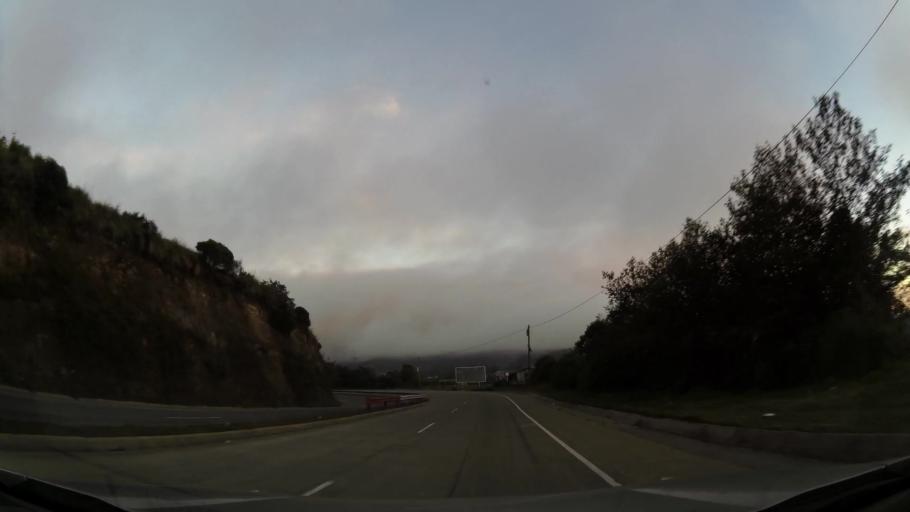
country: GT
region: Solola
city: Concepcion
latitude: 14.8339
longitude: -91.0973
